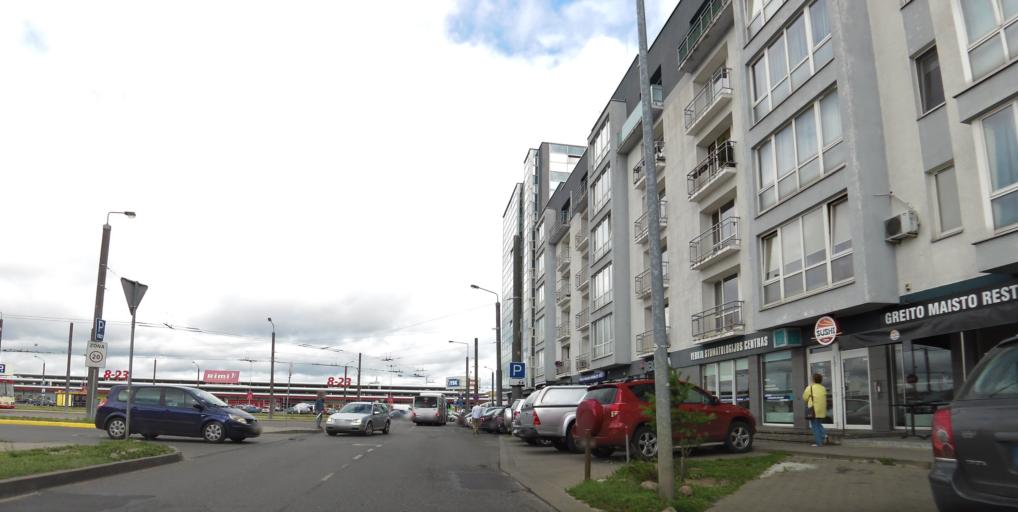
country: LT
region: Vilnius County
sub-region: Vilnius
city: Vilnius
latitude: 54.7104
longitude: 25.3029
